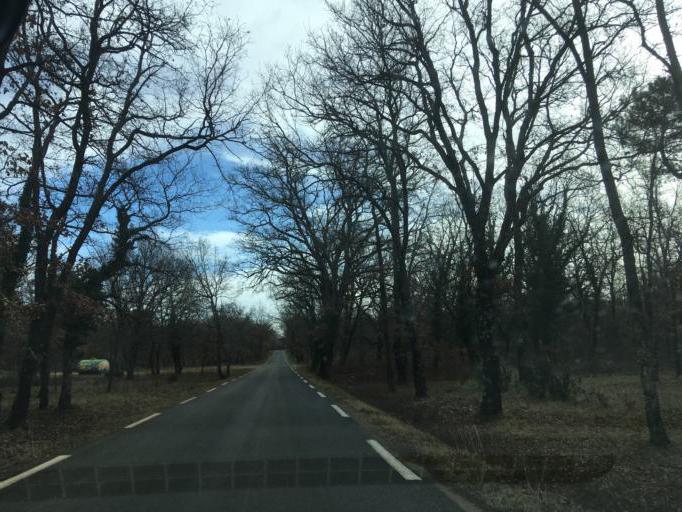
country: FR
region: Provence-Alpes-Cote d'Azur
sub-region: Departement du Var
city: Bras
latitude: 43.4516
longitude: 5.9785
